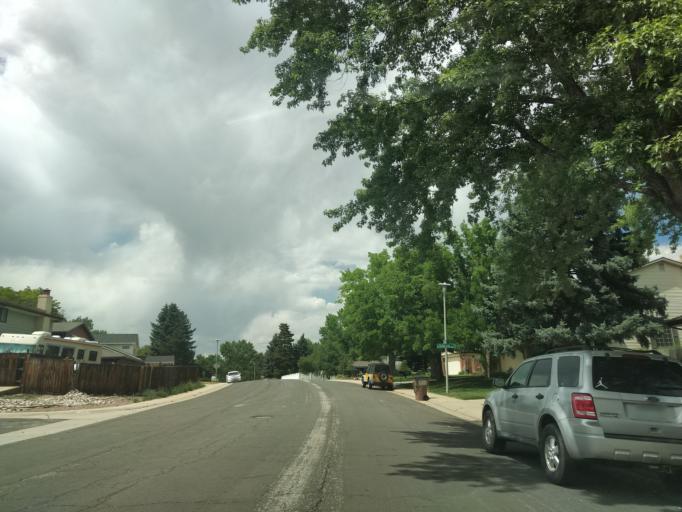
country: US
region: Colorado
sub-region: Jefferson County
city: Lakewood
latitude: 39.6835
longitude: -105.1242
